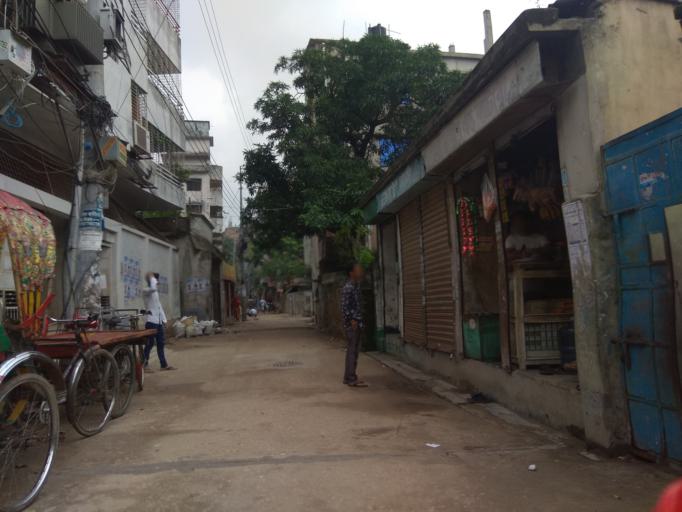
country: BD
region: Dhaka
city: Azimpur
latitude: 23.7934
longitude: 90.3667
